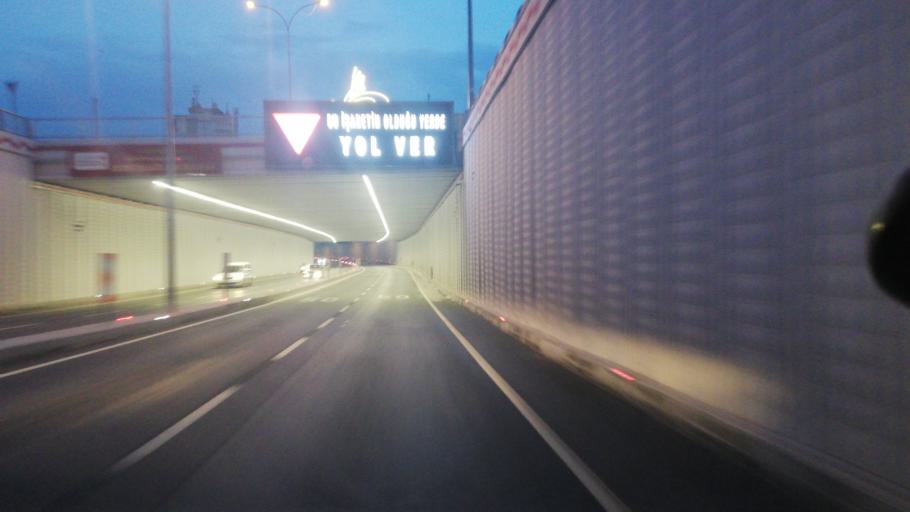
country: TR
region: Kahramanmaras
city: Kahramanmaras
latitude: 37.5848
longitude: 36.9033
